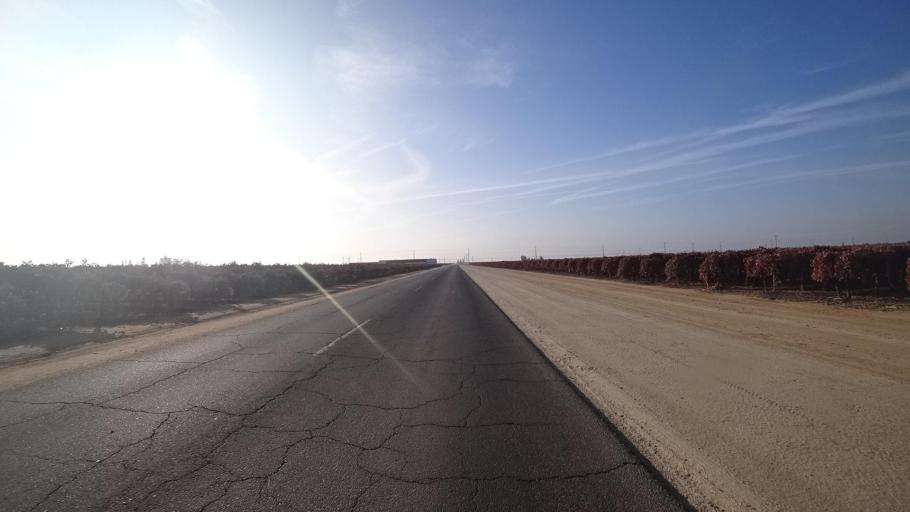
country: US
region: California
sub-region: Kern County
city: Delano
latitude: 35.7795
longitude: -119.1875
